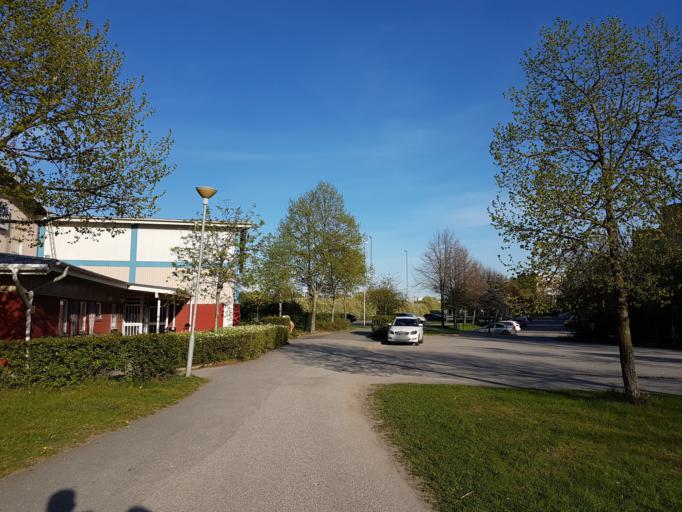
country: SE
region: Stockholm
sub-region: Solna Kommun
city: Rasunda
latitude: 59.3770
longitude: 17.9756
